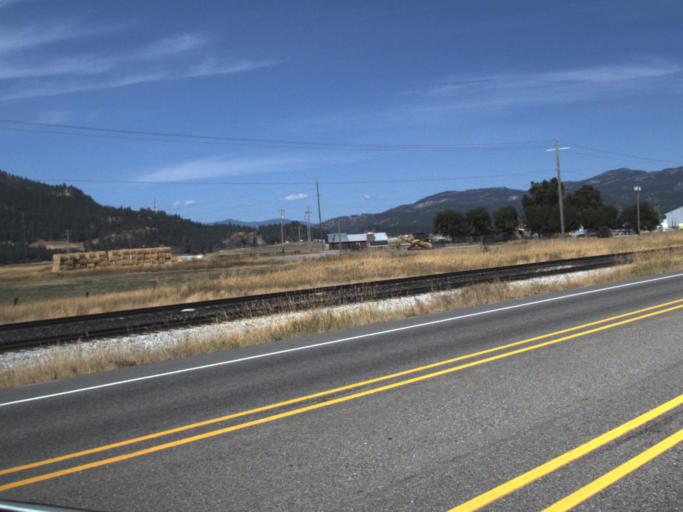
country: US
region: Washington
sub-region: Stevens County
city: Chewelah
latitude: 48.2460
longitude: -117.7152
